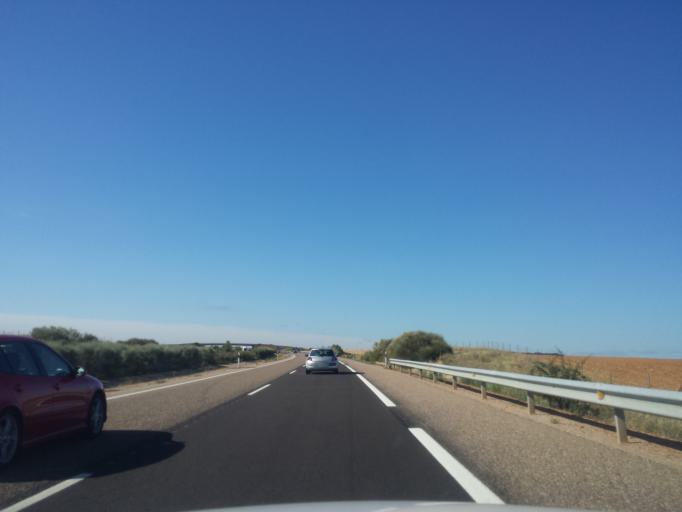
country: ES
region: Castille and Leon
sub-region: Provincia de Zamora
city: Matilla de Arzon
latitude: 42.1140
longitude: -5.6584
